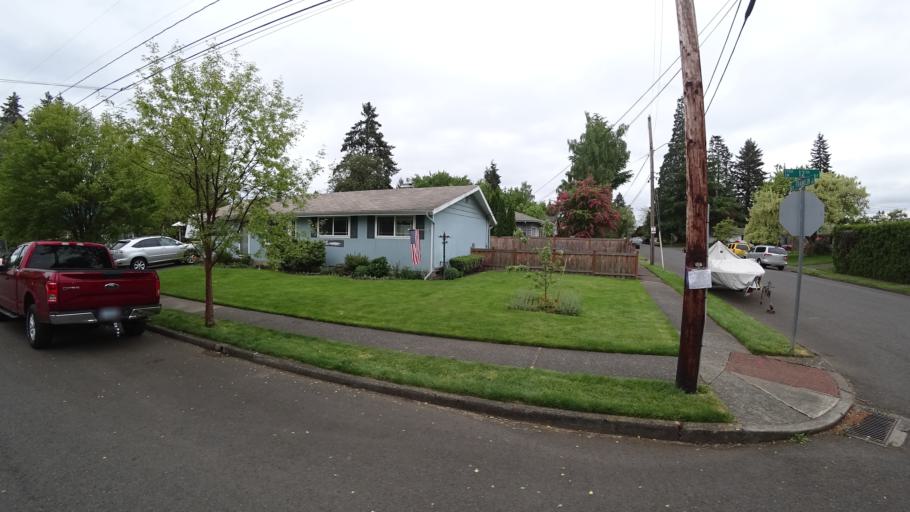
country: US
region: Oregon
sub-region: Washington County
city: Beaverton
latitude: 45.4788
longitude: -122.8015
